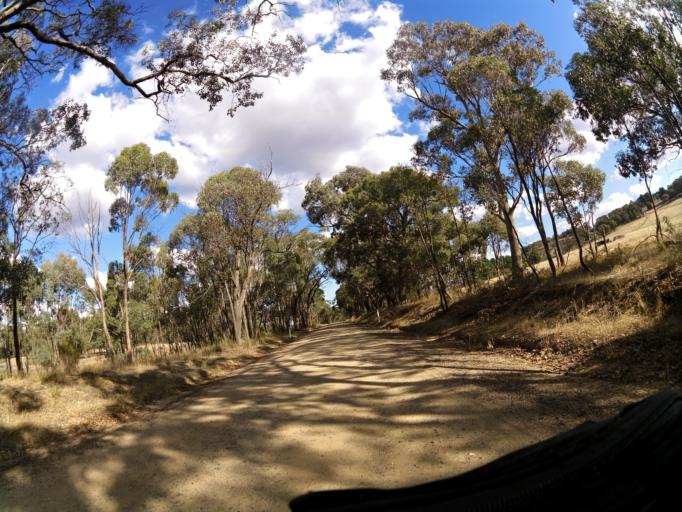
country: AU
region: Victoria
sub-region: Greater Bendigo
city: Kennington
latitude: -36.9968
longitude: 144.8126
